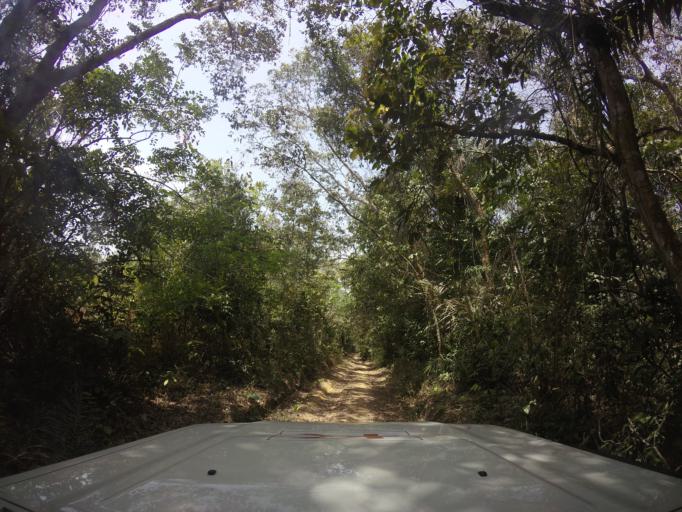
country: LR
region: Grand Cape Mount
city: Robertsport
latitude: 6.9467
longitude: -11.3891
